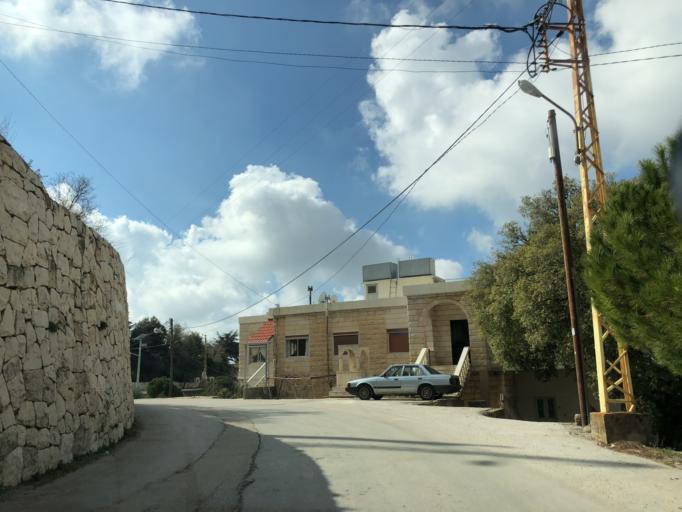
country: LB
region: Liban-Nord
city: Amioun
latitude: 34.2019
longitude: 35.8225
